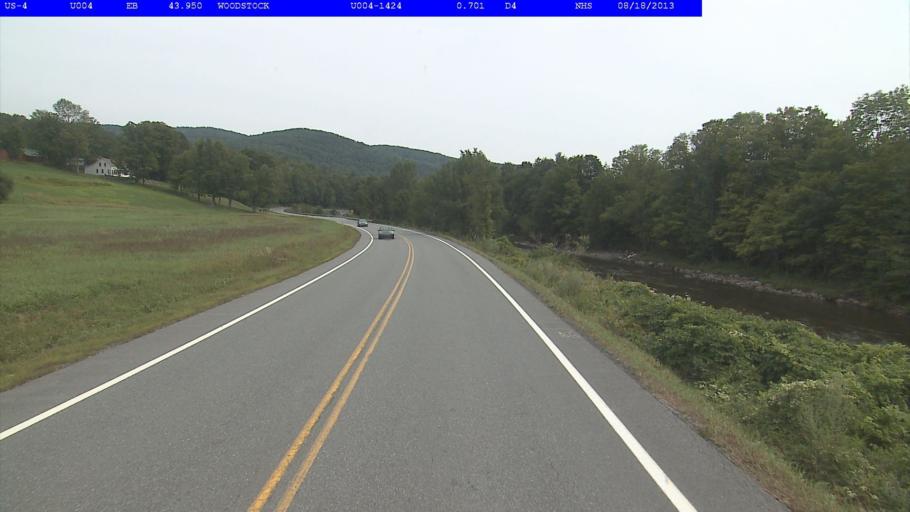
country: US
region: Vermont
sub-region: Windsor County
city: Woodstock
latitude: 43.5906
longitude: -72.6090
